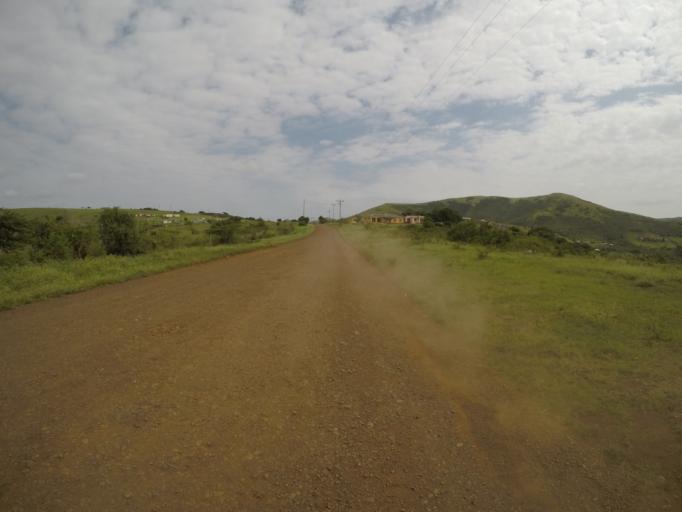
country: ZA
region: KwaZulu-Natal
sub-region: uThungulu District Municipality
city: Empangeni
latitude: -28.6183
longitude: 31.9031
